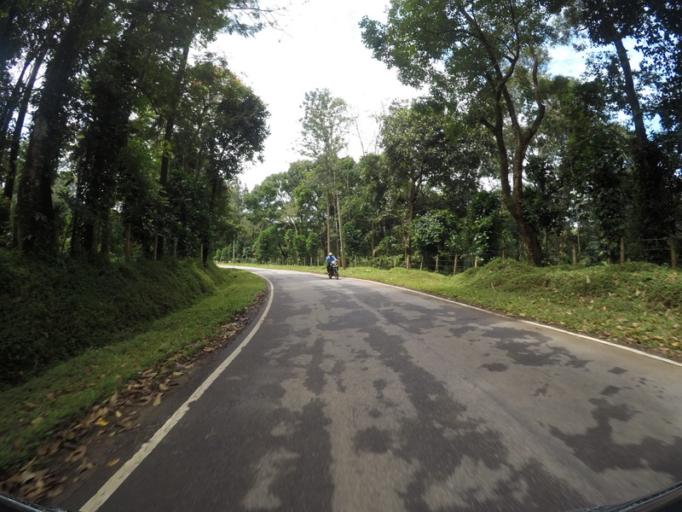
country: IN
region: Karnataka
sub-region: Kodagu
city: Suntikoppa
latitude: 12.4862
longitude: 75.8262
